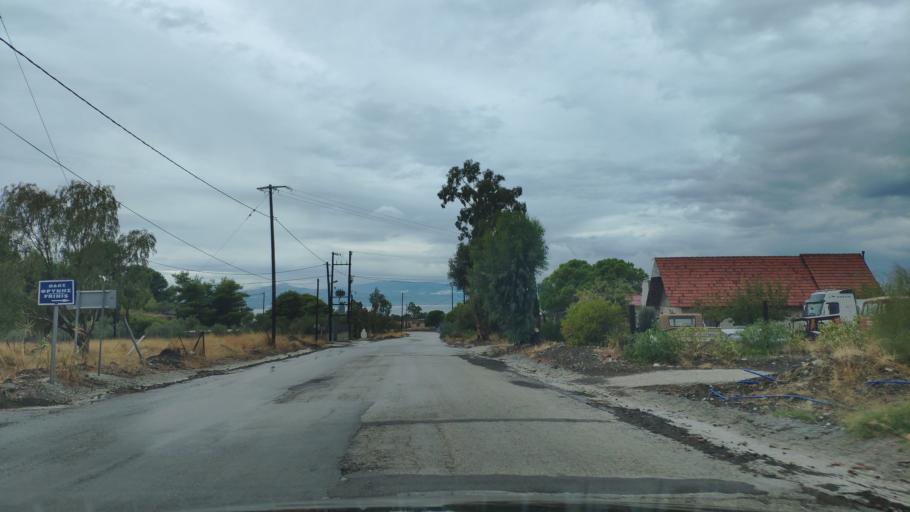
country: GR
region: Peloponnese
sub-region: Nomos Korinthias
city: Loutraki
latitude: 37.9647
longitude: 23.0009
